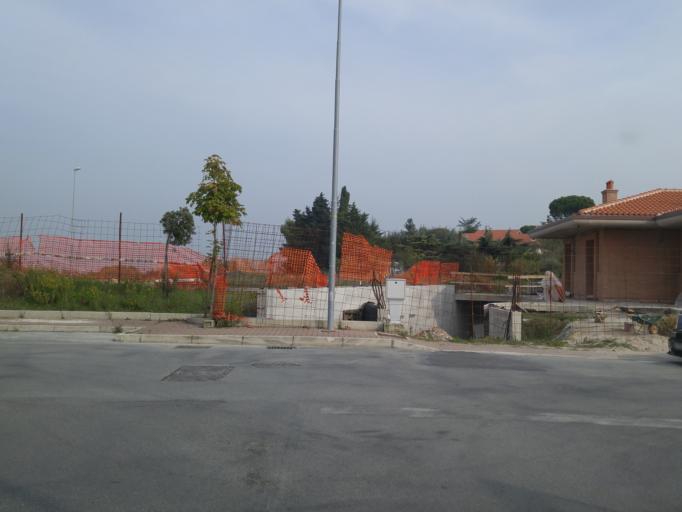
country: IT
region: The Marches
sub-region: Provincia di Pesaro e Urbino
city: Lucrezia
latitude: 43.7720
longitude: 12.9290
